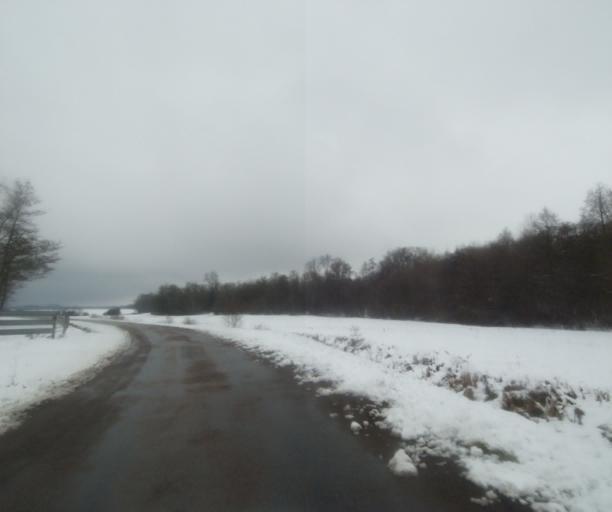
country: FR
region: Champagne-Ardenne
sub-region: Departement de la Haute-Marne
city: Laneuville-a-Remy
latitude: 48.4627
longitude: 4.8297
